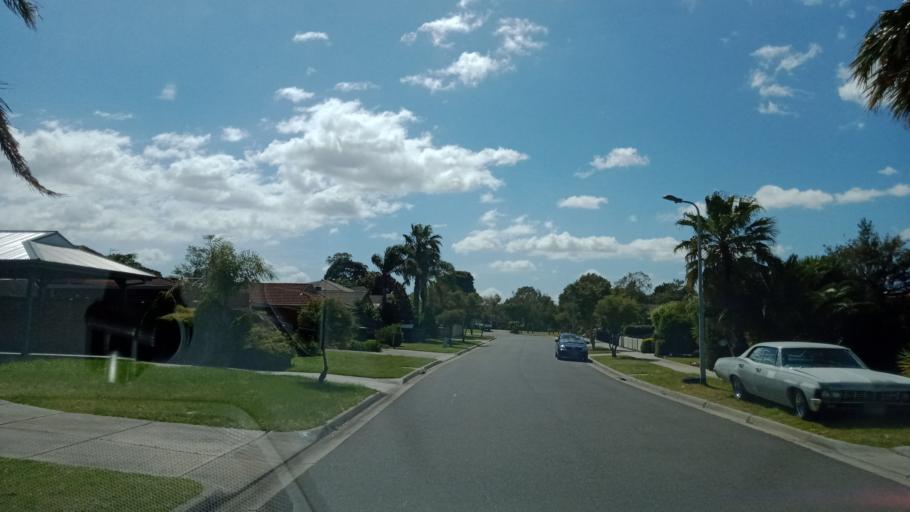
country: AU
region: Victoria
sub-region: Kingston
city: Chelsea Heights
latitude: -38.0383
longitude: 145.1319
